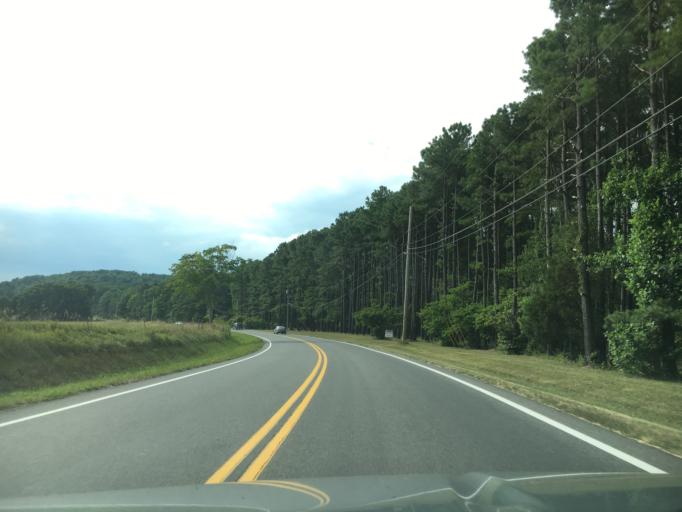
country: US
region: Virginia
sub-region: Campbell County
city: Rustburg
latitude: 37.2700
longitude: -79.1506
